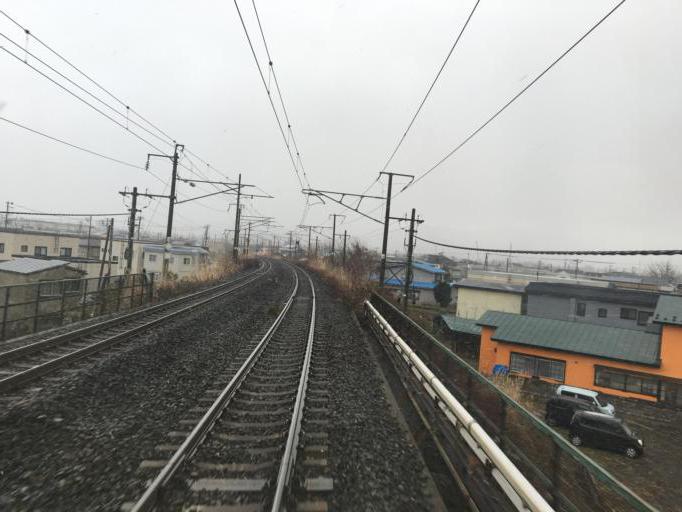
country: JP
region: Aomori
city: Aomori Shi
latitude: 40.8056
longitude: 140.7706
